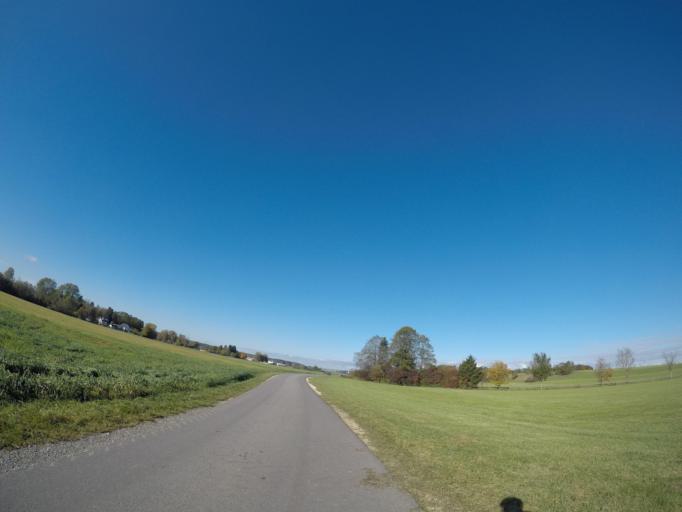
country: DE
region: Baden-Wuerttemberg
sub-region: Tuebingen Region
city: Saulgau
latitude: 48.0272
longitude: 9.5147
